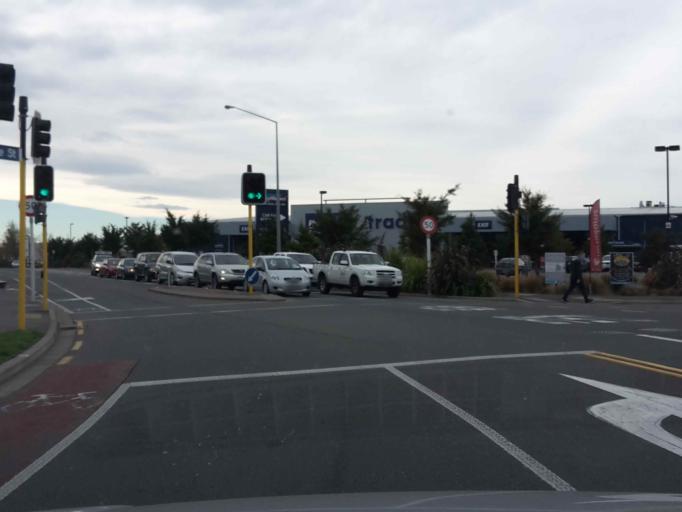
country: NZ
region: Canterbury
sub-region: Christchurch City
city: Christchurch
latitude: -43.5367
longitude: 172.6070
